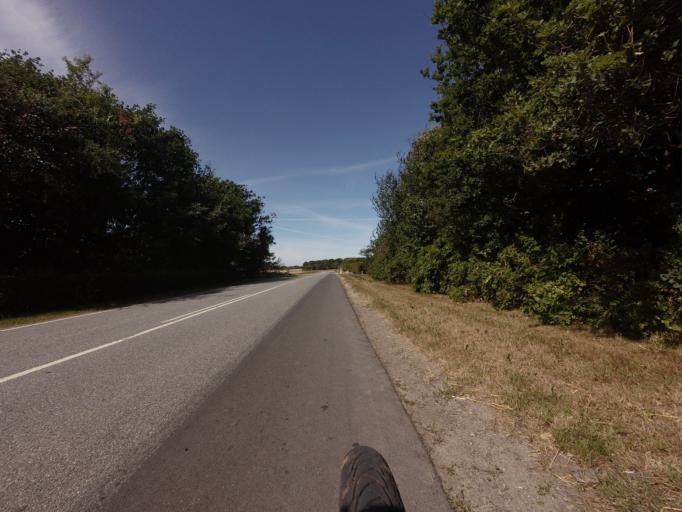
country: DK
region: North Denmark
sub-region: Hjorring Kommune
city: Vra
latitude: 57.3310
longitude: 9.8207
